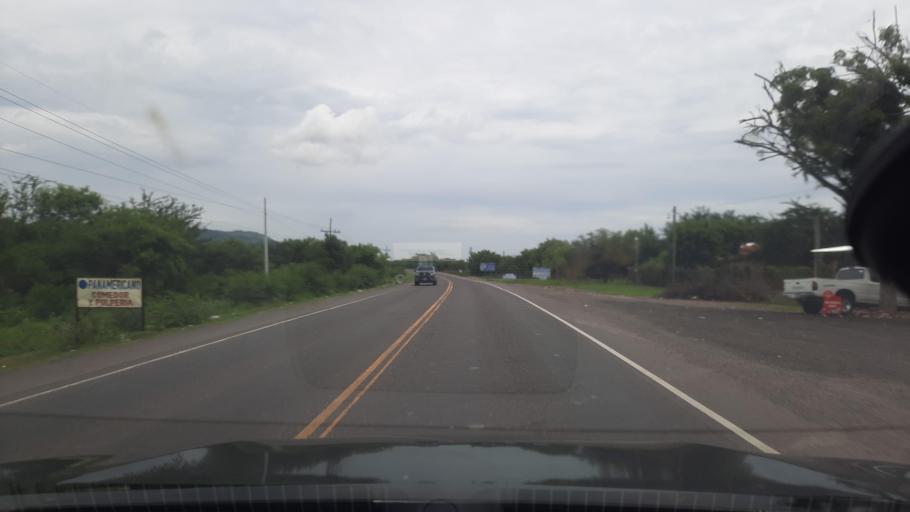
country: HN
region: Valle
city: Jicaro Galan
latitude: 13.5212
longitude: -87.4391
